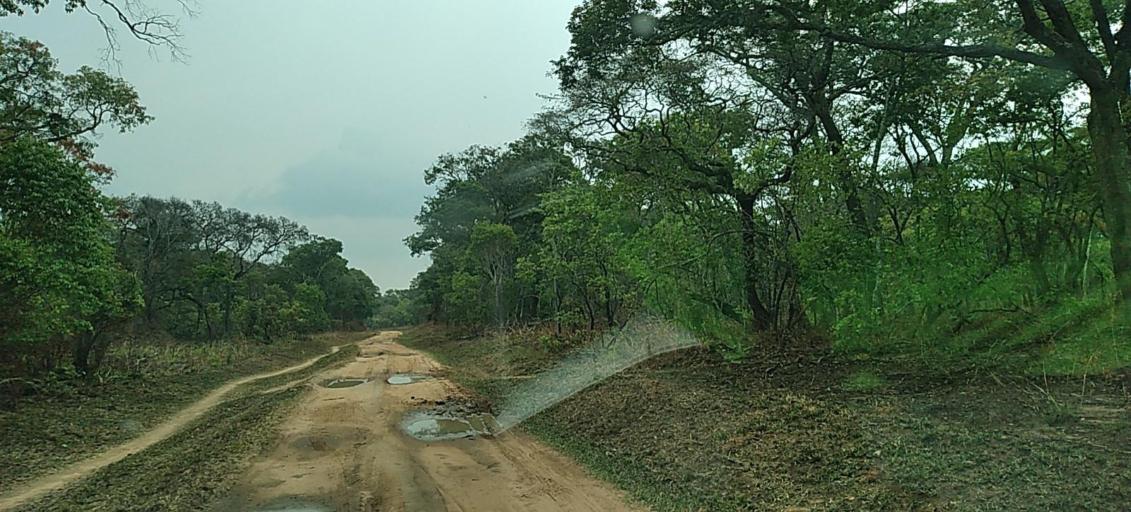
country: ZM
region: North-Western
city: Mwinilunga
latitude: -11.4664
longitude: 24.4733
